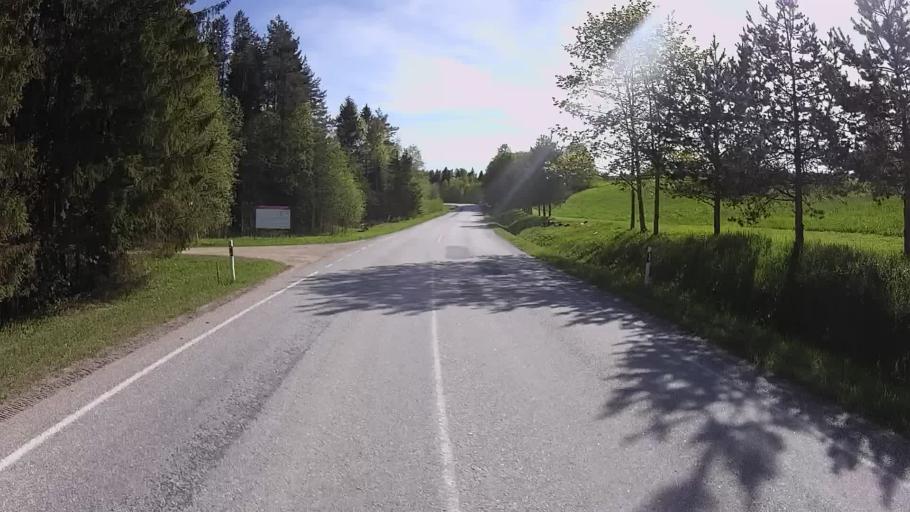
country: EE
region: Vorumaa
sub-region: Antsla vald
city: Vana-Antsla
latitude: 58.0128
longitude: 26.4975
